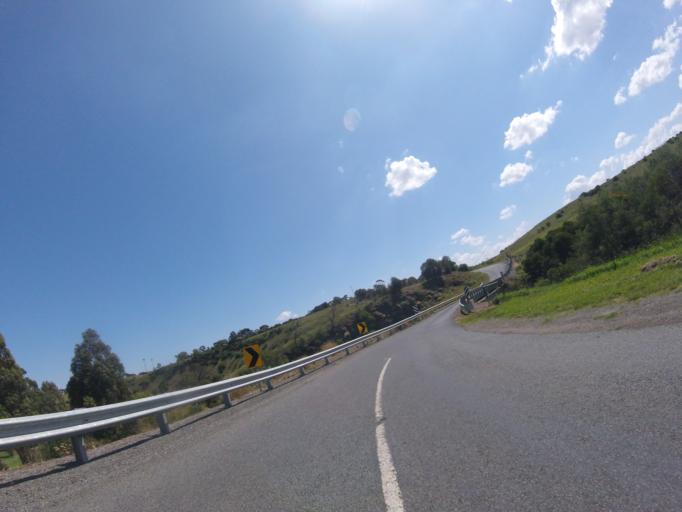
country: AU
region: Victoria
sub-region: Hume
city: Sunbury
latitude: -37.5844
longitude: 144.7689
